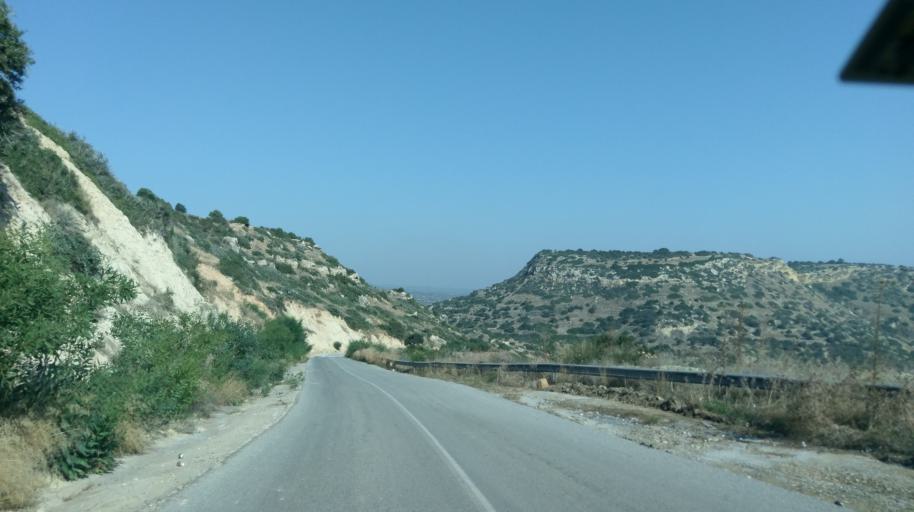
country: CY
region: Ammochostos
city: Leonarisso
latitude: 35.4921
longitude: 34.2237
